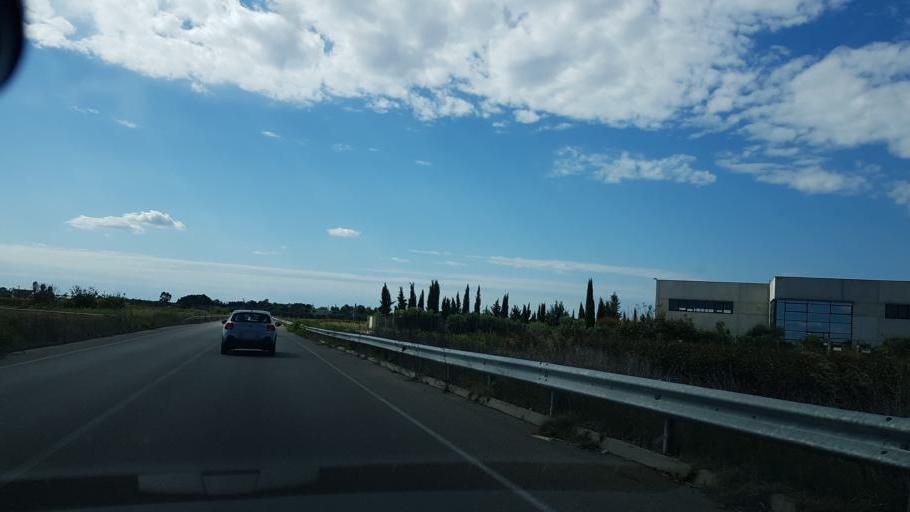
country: IT
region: Apulia
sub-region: Provincia di Lecce
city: Leverano
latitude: 40.2922
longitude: 17.9703
